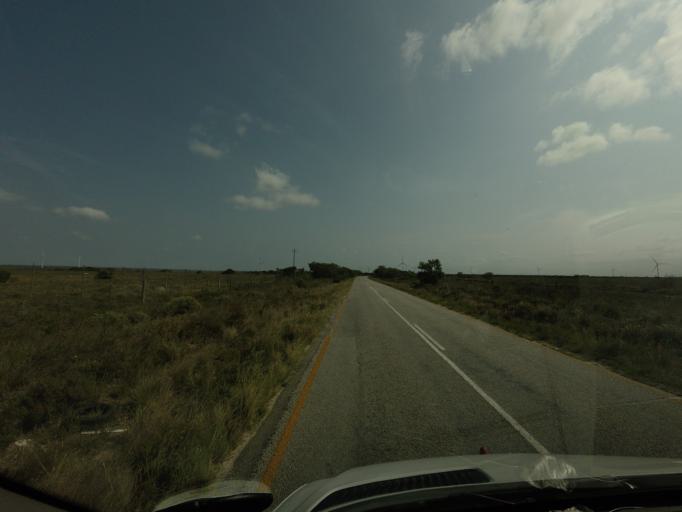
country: ZA
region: Eastern Cape
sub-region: Nelson Mandela Bay Metropolitan Municipality
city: Uitenhage
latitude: -33.6888
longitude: 25.5883
